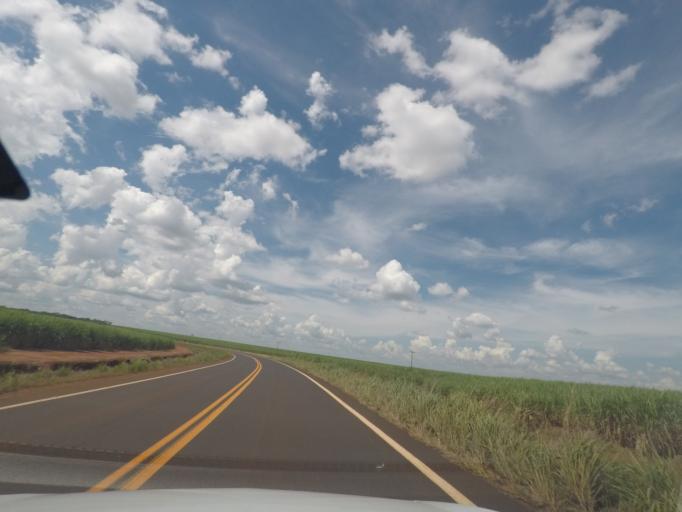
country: BR
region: Minas Gerais
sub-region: Conceicao Das Alagoas
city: Conceicao das Alagoas
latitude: -19.8614
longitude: -48.6021
